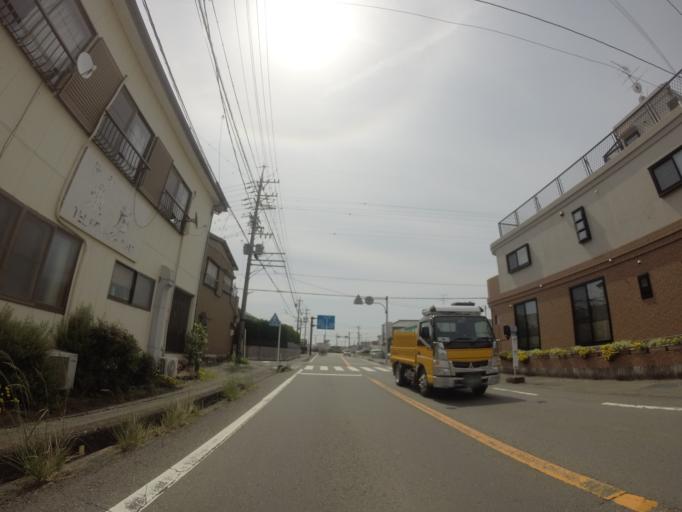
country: JP
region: Shizuoka
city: Fujieda
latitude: 34.8169
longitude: 138.2783
